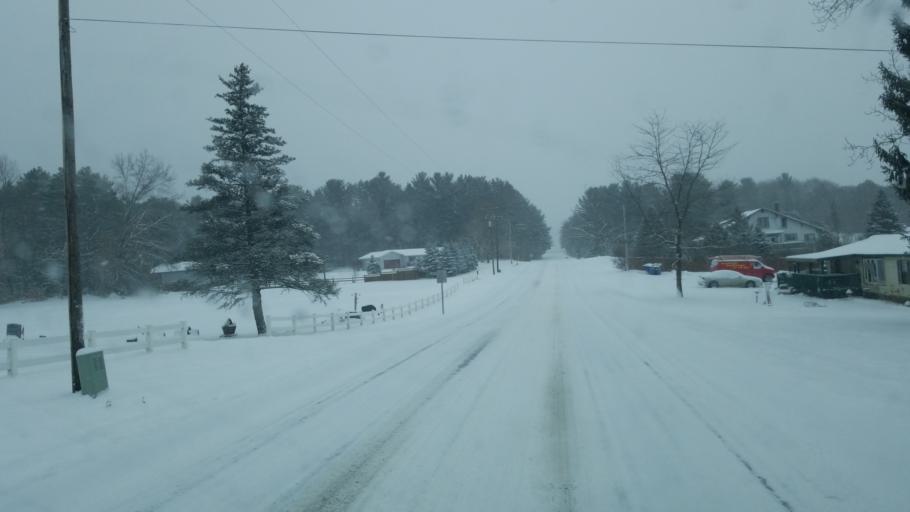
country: US
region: Michigan
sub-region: Mecosta County
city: Big Rapids
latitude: 43.5768
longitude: -85.4431
